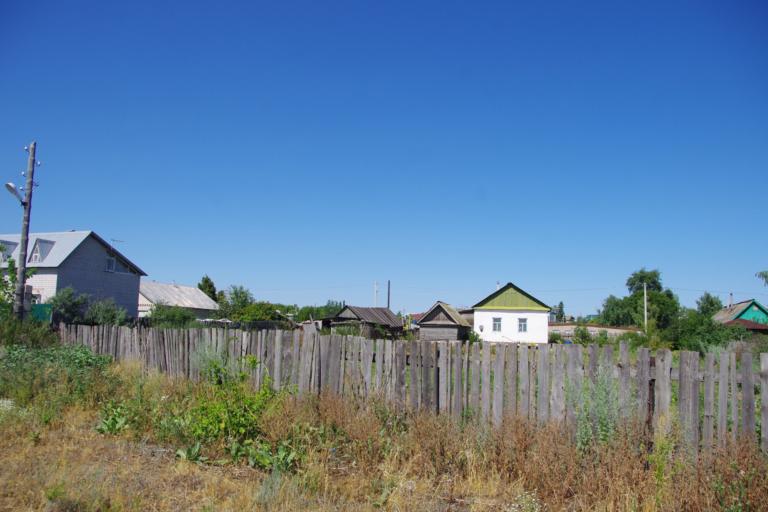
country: RU
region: Samara
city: Rozhdestveno
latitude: 53.2267
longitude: 50.0626
